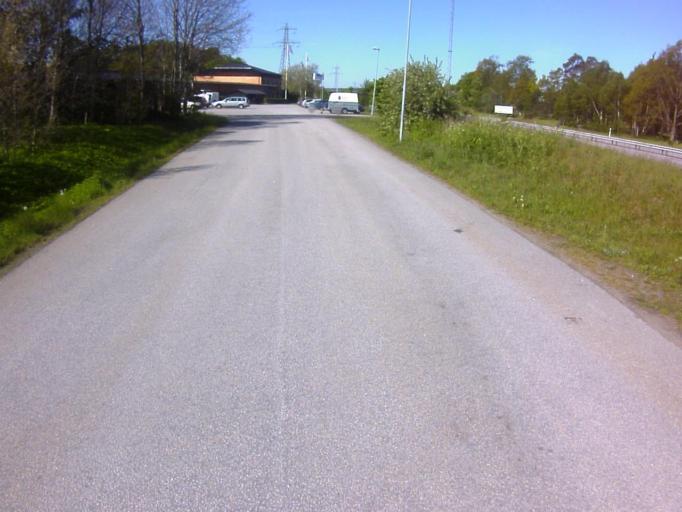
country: SE
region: Blekinge
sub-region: Solvesborgs Kommun
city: Soelvesborg
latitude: 56.0670
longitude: 14.6272
